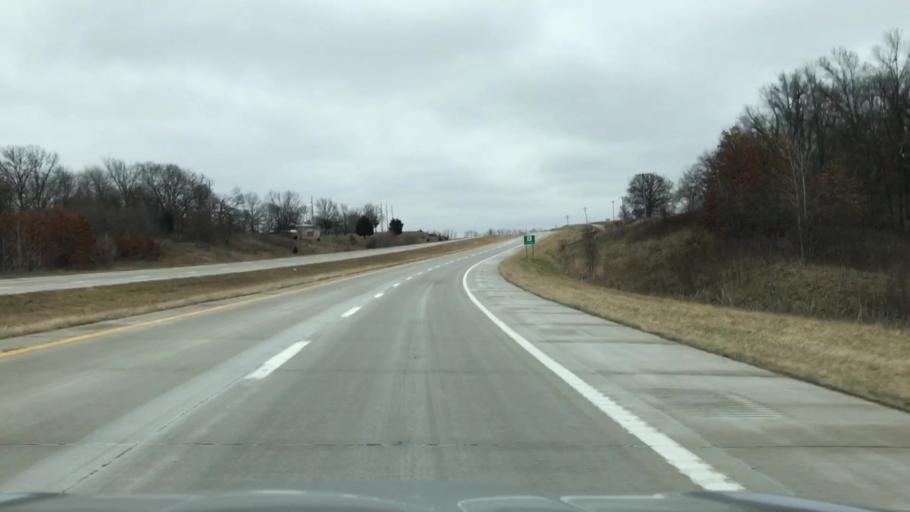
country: US
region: Missouri
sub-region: Livingston County
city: Chillicothe
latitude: 39.7393
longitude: -93.6386
